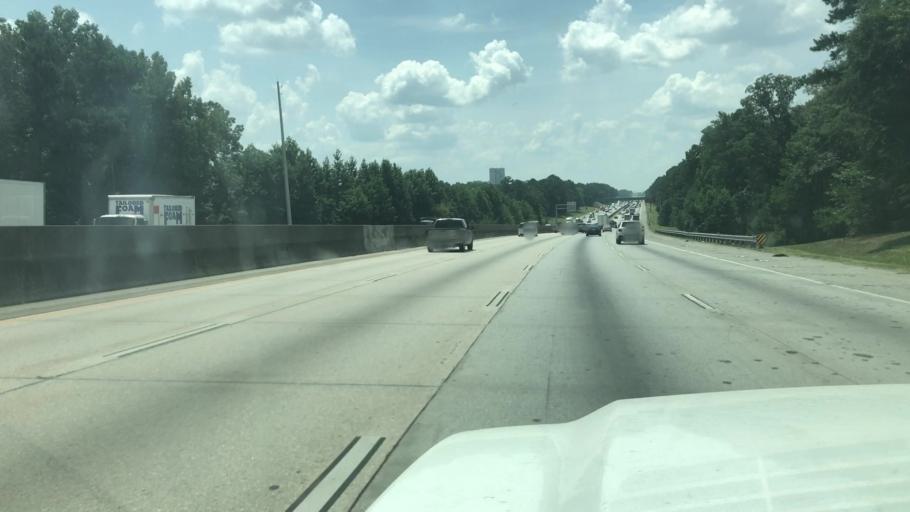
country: US
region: Georgia
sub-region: Fulton County
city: Union City
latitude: 33.5629
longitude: -84.5392
